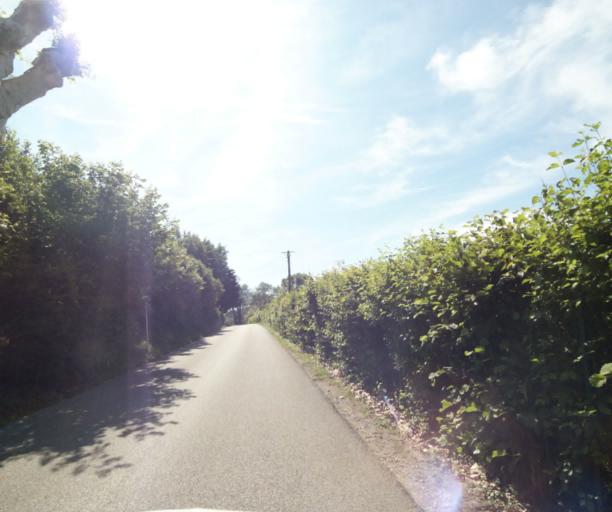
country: FR
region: Rhone-Alpes
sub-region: Departement de la Haute-Savoie
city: Anthy-sur-Leman
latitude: 46.3492
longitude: 6.4035
